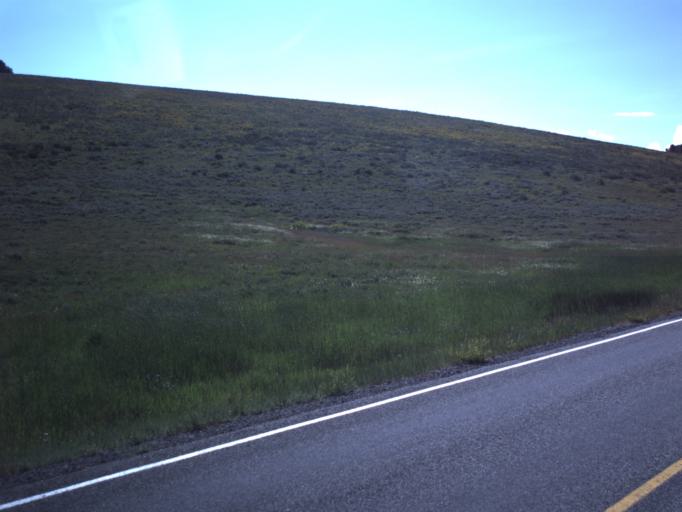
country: US
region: Utah
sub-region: Sanpete County
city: Fairview
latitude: 39.6629
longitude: -111.3016
